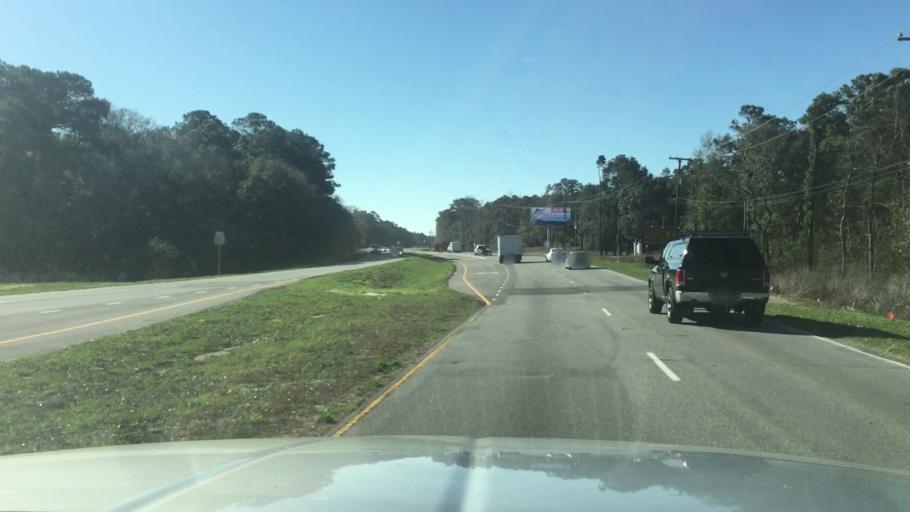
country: US
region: North Carolina
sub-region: New Hanover County
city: Sea Breeze
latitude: 34.0993
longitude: -77.8992
